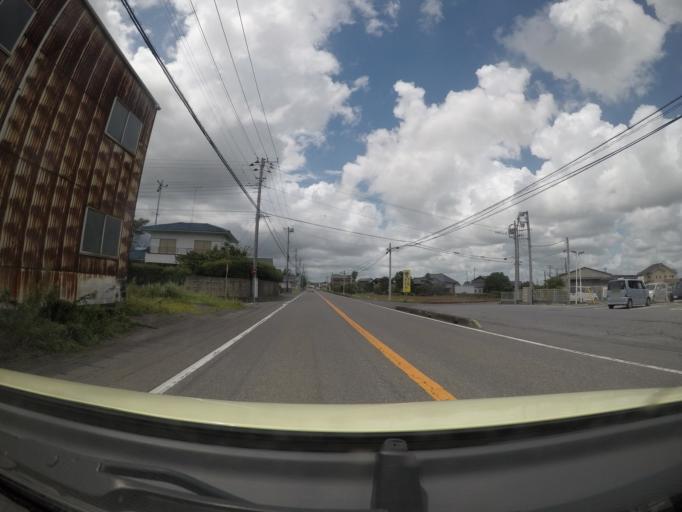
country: JP
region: Ibaraki
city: Mitsukaido
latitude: 36.0529
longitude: 139.9854
